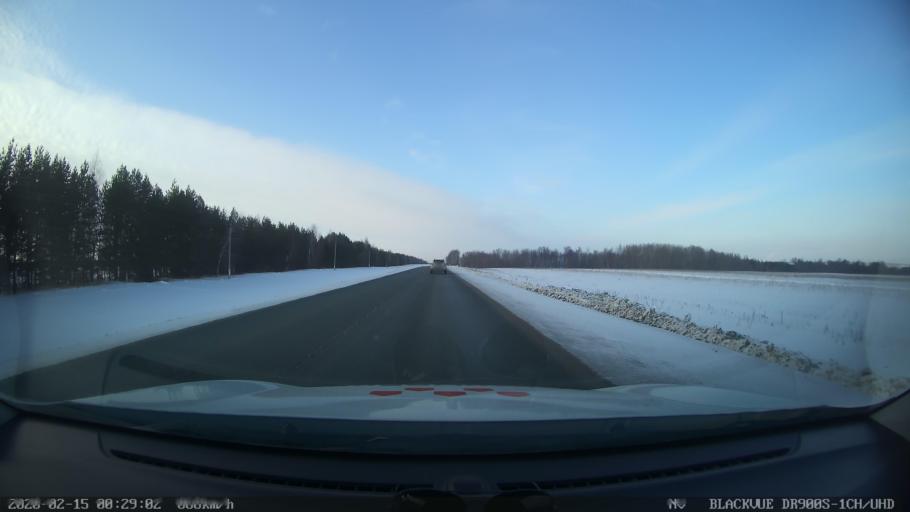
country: RU
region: Tatarstan
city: Verkhniy Uslon
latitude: 55.6473
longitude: 48.8728
